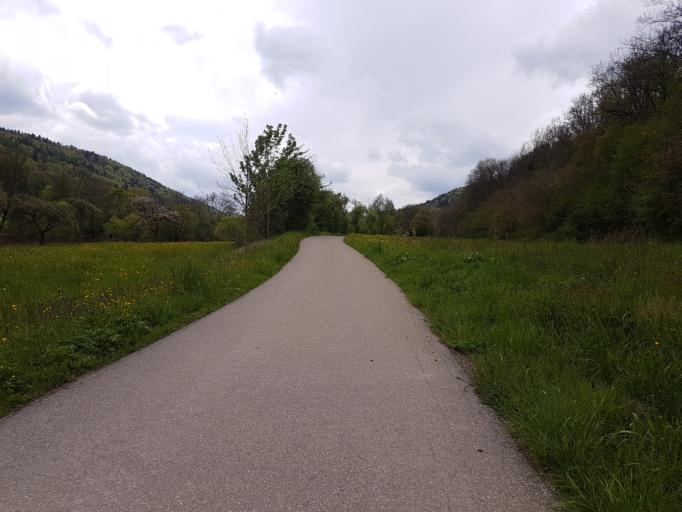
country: DE
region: Baden-Wuerttemberg
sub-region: Freiburg Region
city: Stuhlingen
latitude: 47.7229
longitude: 8.4354
